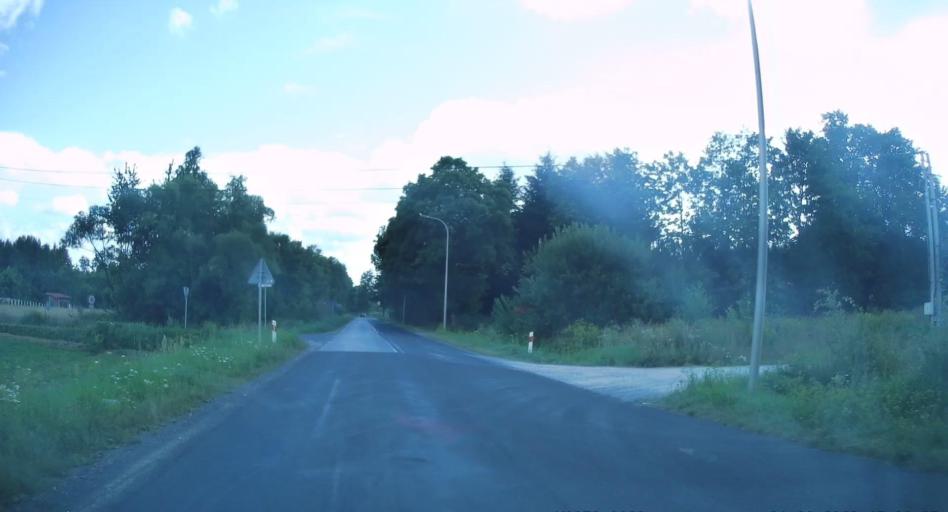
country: PL
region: Swietokrzyskie
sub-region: Powiat kielecki
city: Lagow
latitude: 50.8079
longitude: 21.0794
